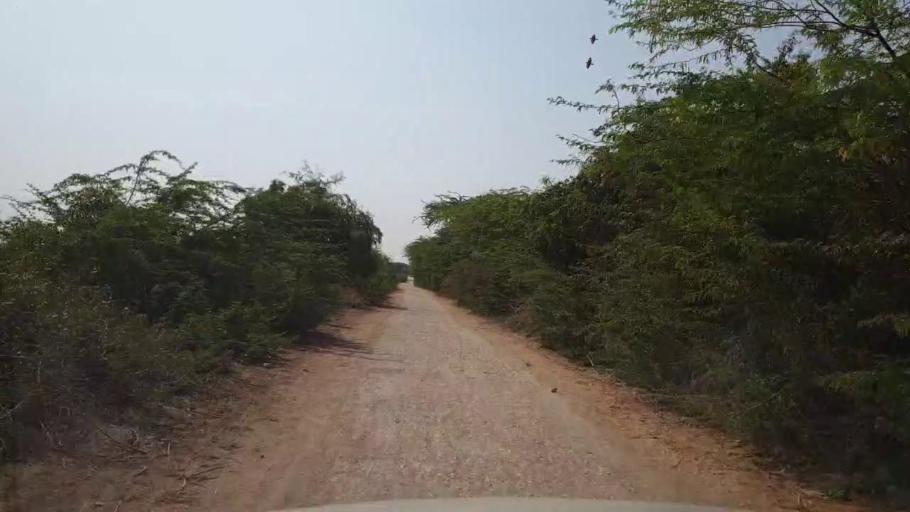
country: PK
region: Sindh
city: Dhoro Naro
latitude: 25.4648
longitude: 69.6339
